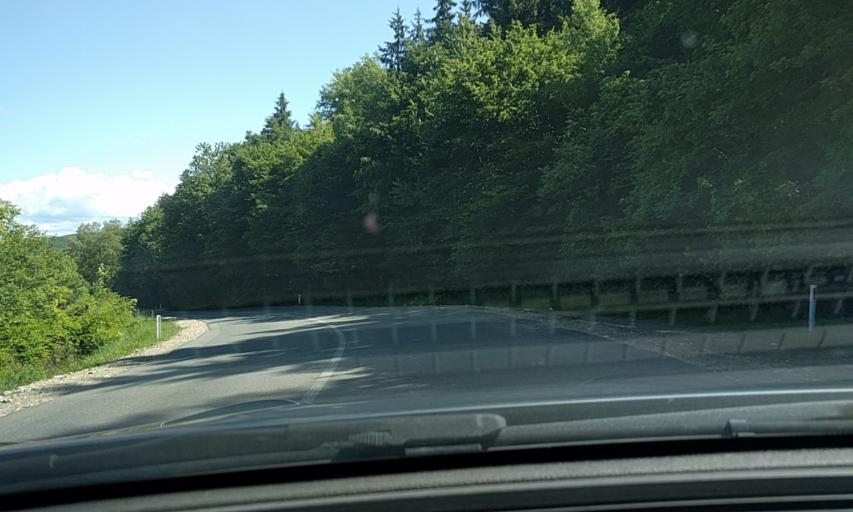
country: RO
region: Bistrita-Nasaud
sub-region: Comuna Dumitra
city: Dumitra
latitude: 47.1918
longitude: 24.4822
